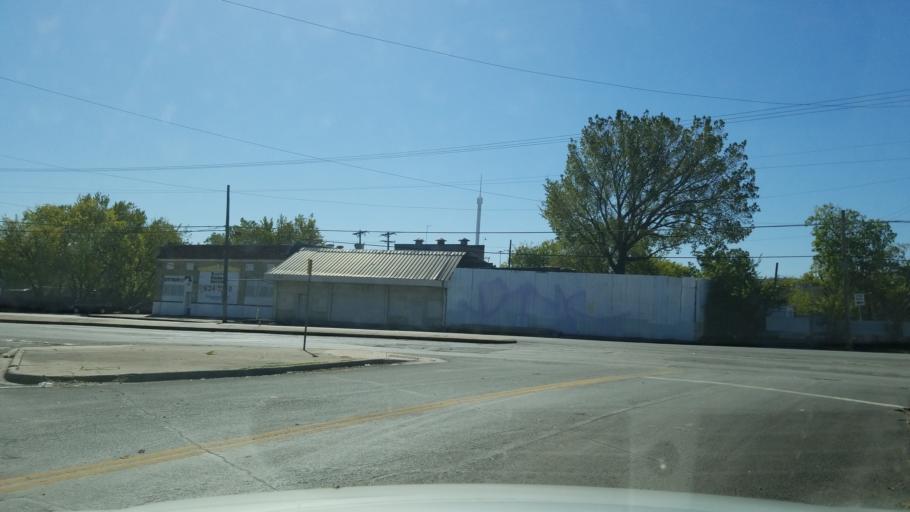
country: US
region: Texas
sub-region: Dallas County
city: Dallas
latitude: 32.7844
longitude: -96.7593
